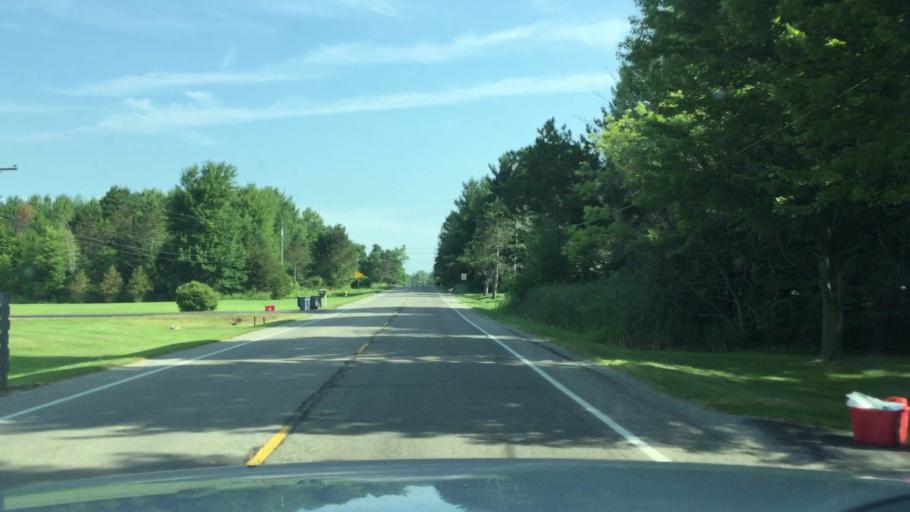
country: US
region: Michigan
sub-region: Genesee County
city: Flushing
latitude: 43.1131
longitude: -83.8728
